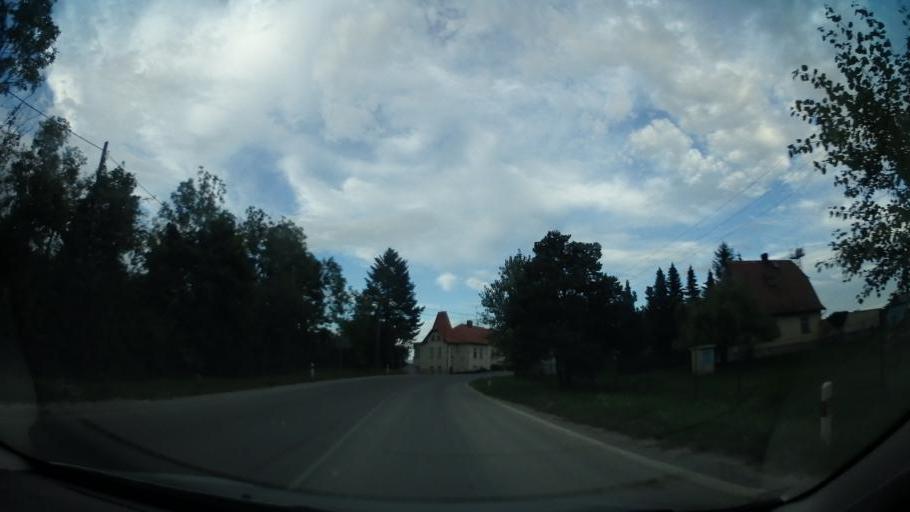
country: CZ
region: Olomoucky
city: Bila Lhota
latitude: 49.7033
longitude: 17.0021
